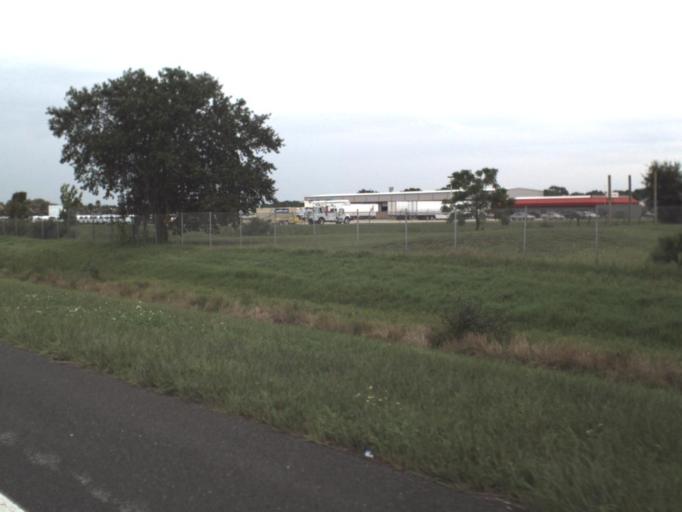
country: US
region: Florida
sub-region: Manatee County
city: Whitfield
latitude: 27.4133
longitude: -82.5327
